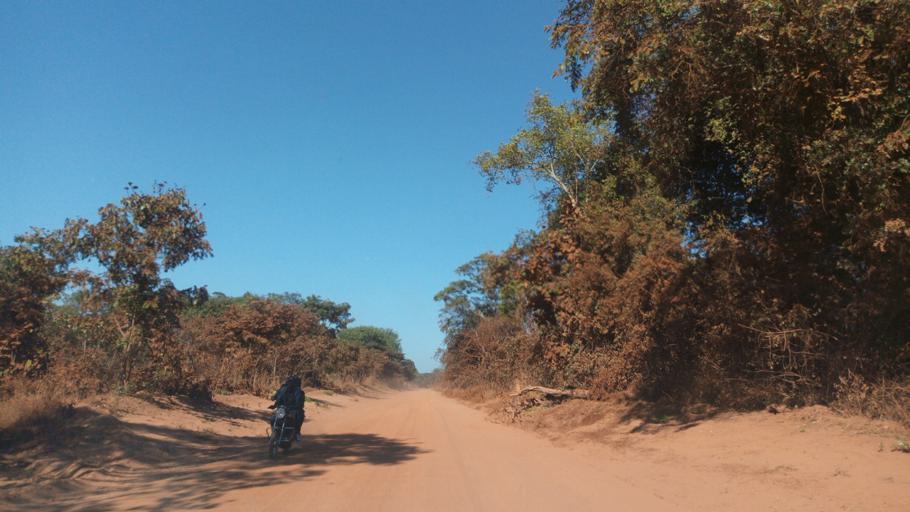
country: ZM
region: Luapula
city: Mwense
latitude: -10.7499
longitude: 28.3254
